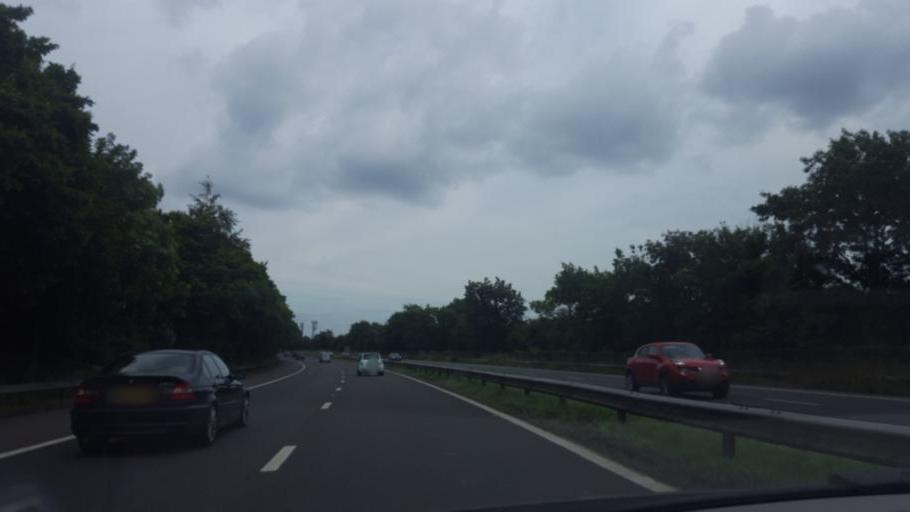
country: GB
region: England
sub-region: Royal Borough of Windsor and Maidenhead
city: White Waltham
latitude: 51.5137
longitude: -0.7591
